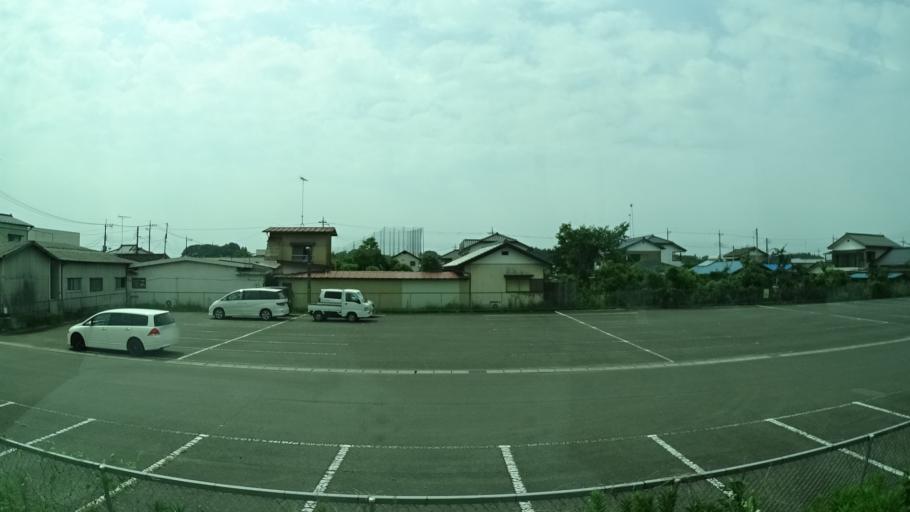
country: JP
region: Tochigi
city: Mashiko
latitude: 36.4620
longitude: 140.0881
